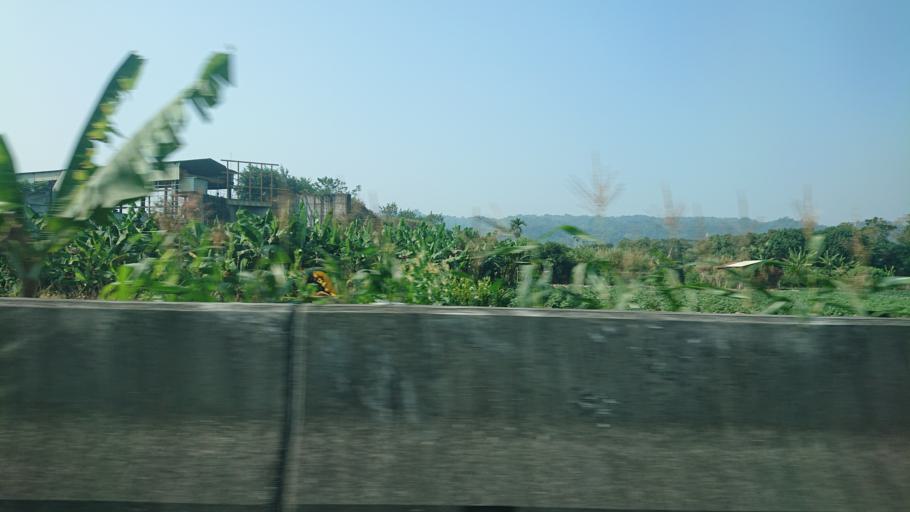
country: TW
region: Taiwan
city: Lugu
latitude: 23.7617
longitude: 120.6618
